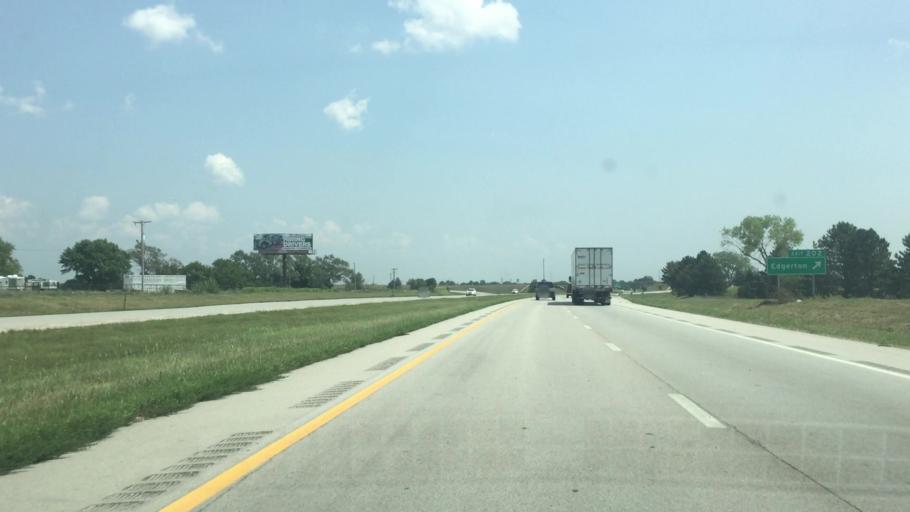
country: US
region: Kansas
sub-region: Johnson County
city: Edgerton
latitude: 38.7440
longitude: -95.0075
